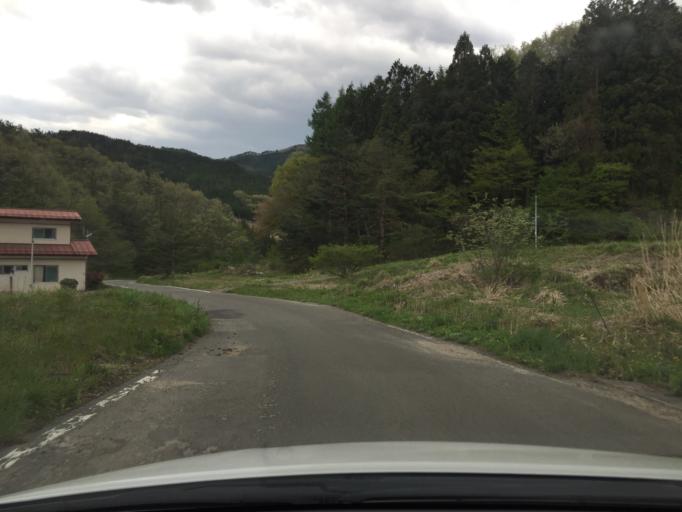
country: JP
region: Fukushima
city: Yanagawamachi-saiwaicho
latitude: 37.7576
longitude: 140.6988
